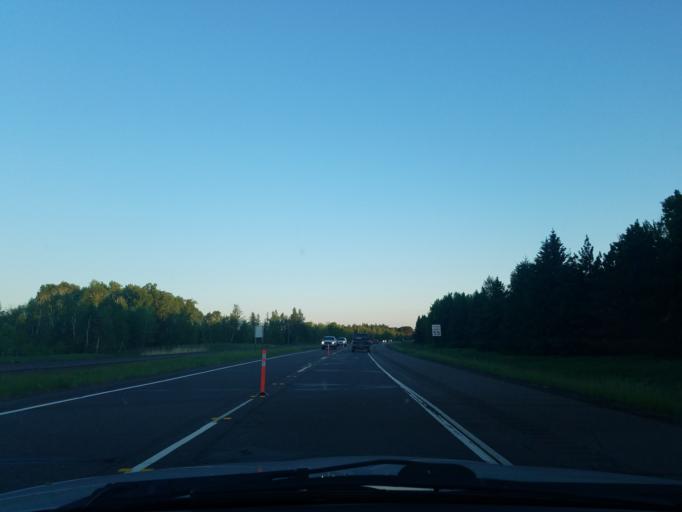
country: US
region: Minnesota
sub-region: Pine County
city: Sandstone
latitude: 46.2897
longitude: -92.8200
